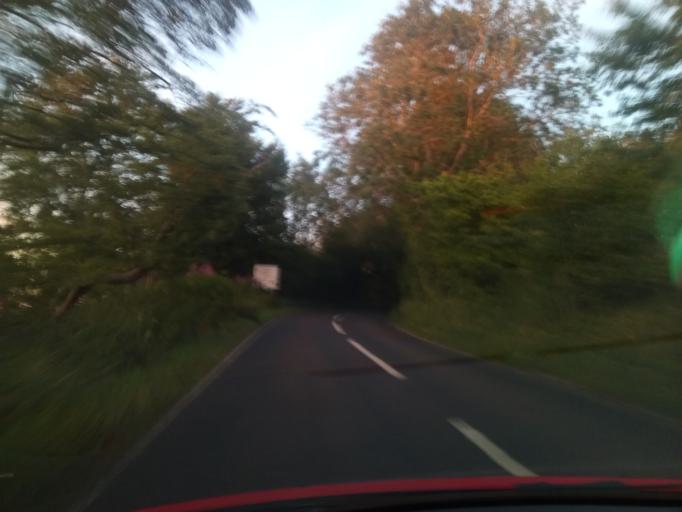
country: GB
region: England
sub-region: Northumberland
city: Bardon Mill
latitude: 54.9297
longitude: -2.3076
